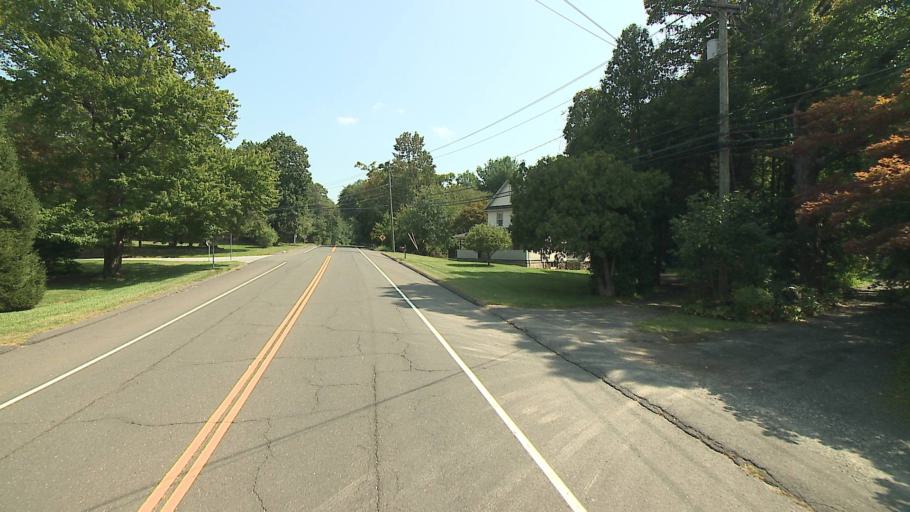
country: US
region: Connecticut
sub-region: Fairfield County
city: Georgetown
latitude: 41.2536
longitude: -73.4244
